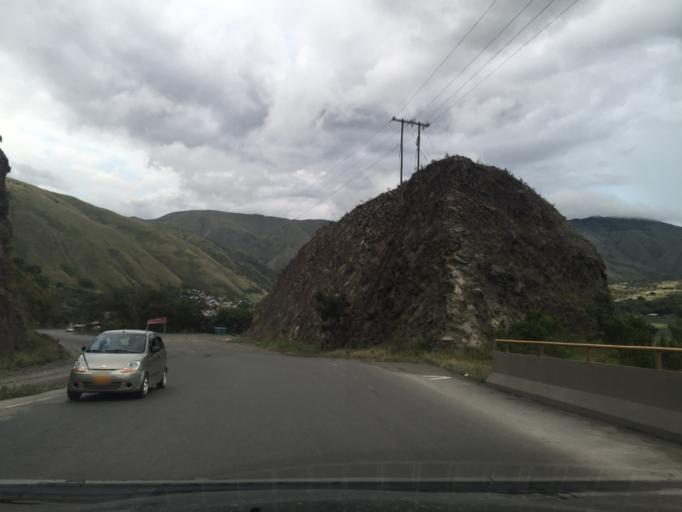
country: CO
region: Valle del Cauca
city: Dagua
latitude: 3.7678
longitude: -76.6777
